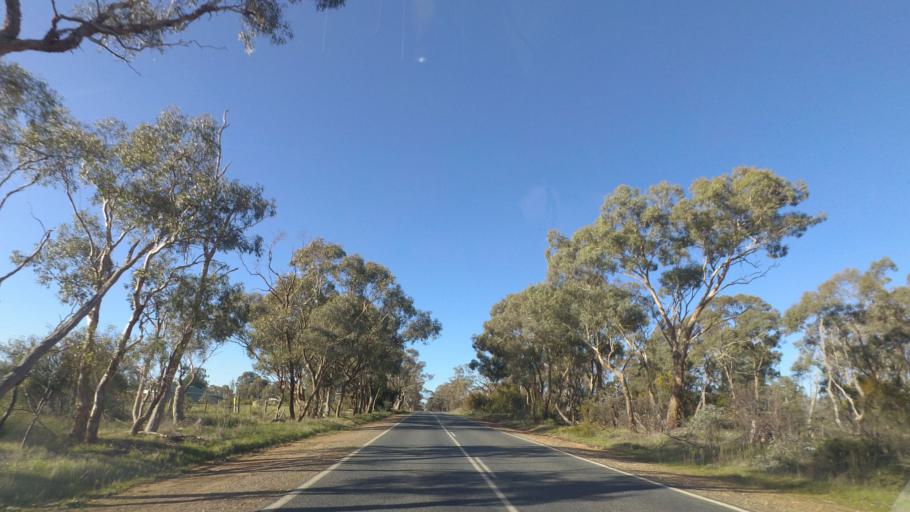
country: AU
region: Victoria
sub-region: Greater Bendigo
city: Epsom
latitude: -36.6772
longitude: 144.3872
